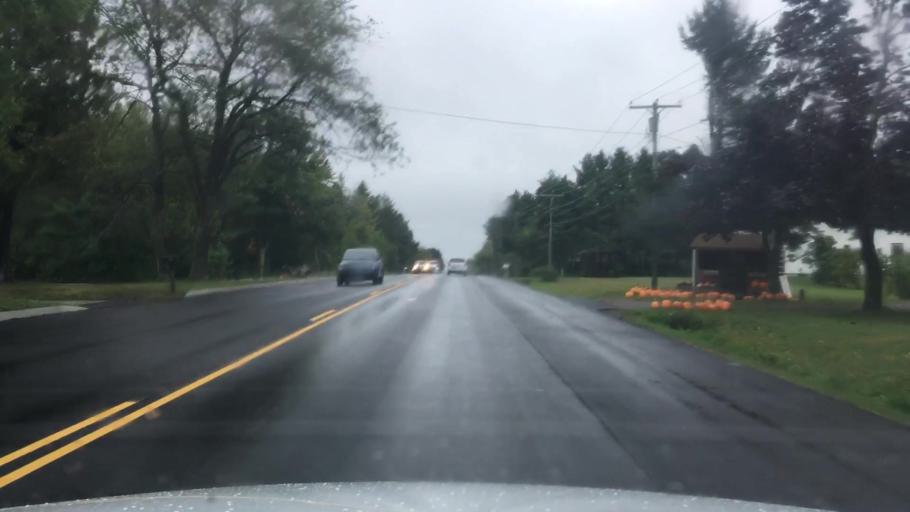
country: US
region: Maine
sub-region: Penobscot County
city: Hampden
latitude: 44.7633
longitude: -68.8505
